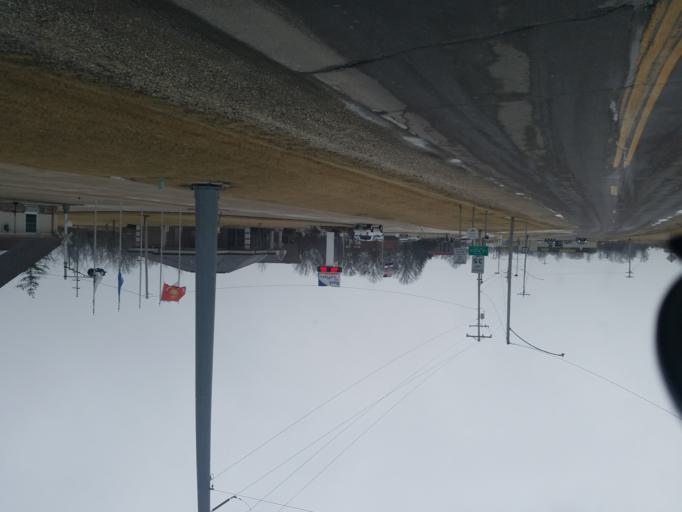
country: US
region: Missouri
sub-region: Macon County
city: La Plata
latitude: 40.0345
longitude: -92.4893
